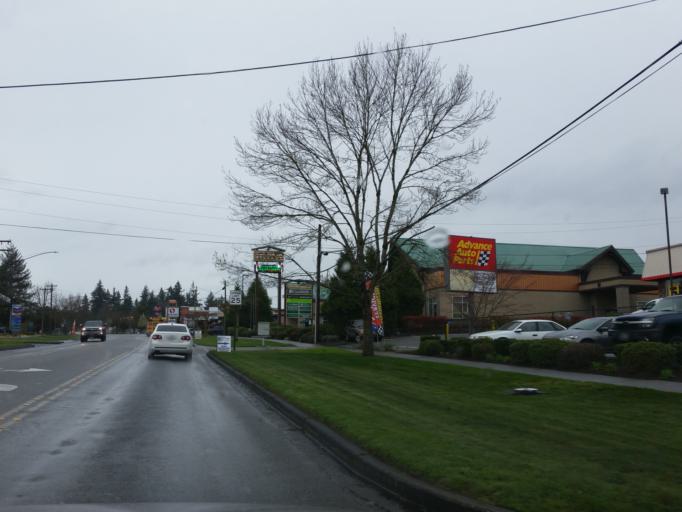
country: US
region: Washington
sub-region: Snohomish County
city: Snohomish
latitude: 47.9244
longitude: -122.0978
